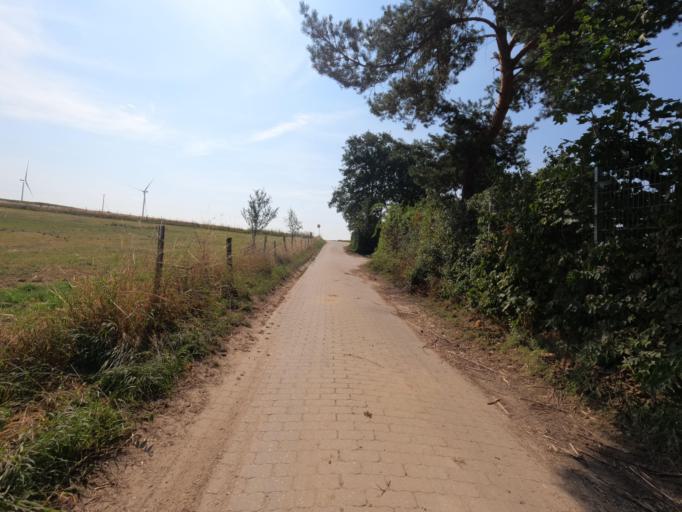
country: DE
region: North Rhine-Westphalia
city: Julich
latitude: 50.9798
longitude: 6.3610
